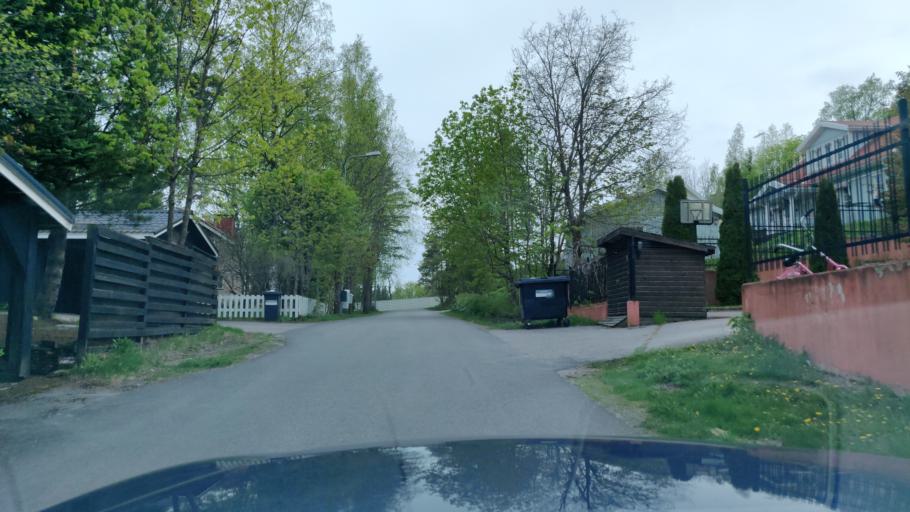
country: FI
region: Uusimaa
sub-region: Helsinki
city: Nurmijaervi
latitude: 60.3726
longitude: 24.7494
